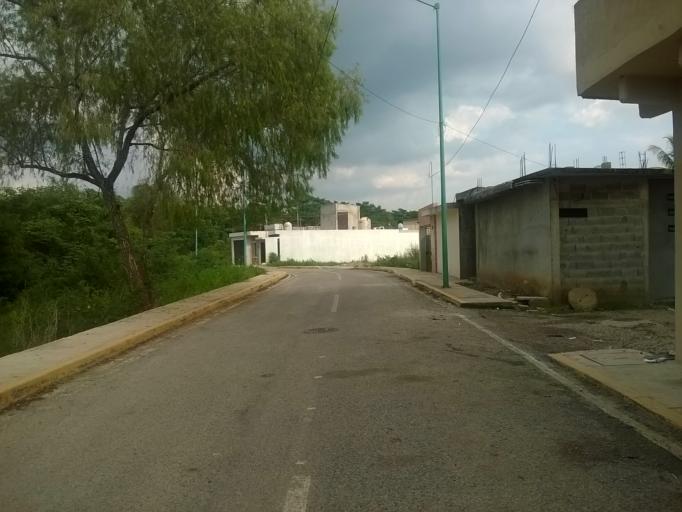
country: MX
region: Tabasco
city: Jalapa
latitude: 17.7249
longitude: -92.8102
